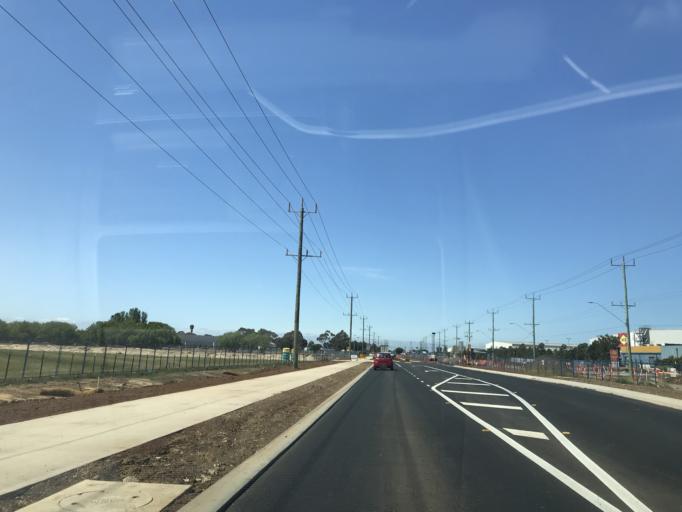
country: AU
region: Victoria
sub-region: Hobsons Bay
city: Laverton
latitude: -37.8425
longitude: 144.7741
